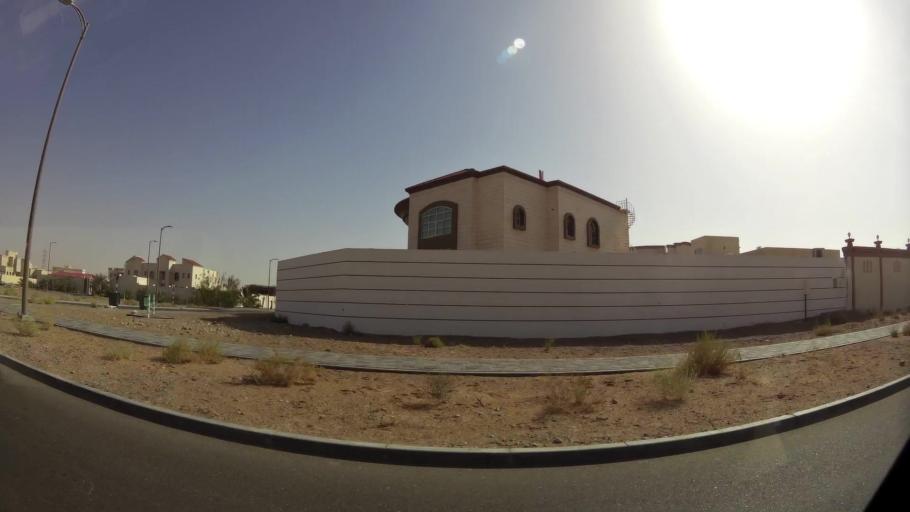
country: OM
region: Al Buraimi
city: Al Buraymi
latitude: 24.3567
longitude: 55.7907
